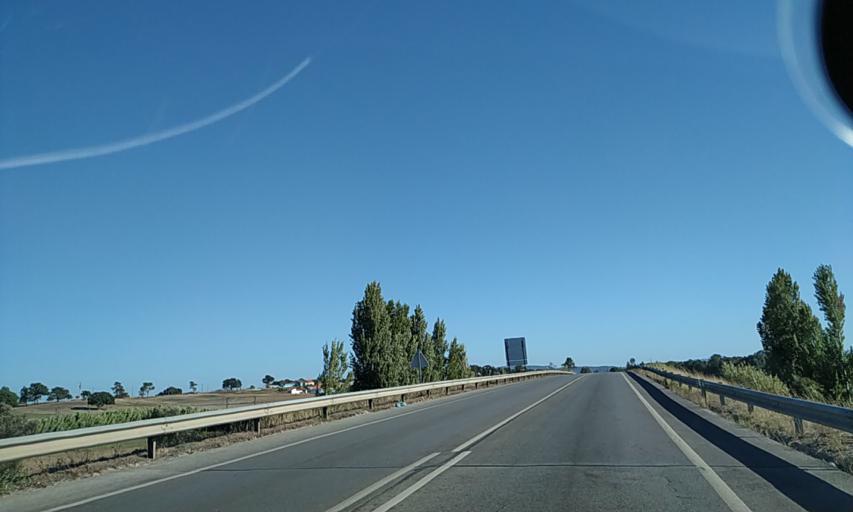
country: PT
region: Setubal
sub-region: Moita
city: Moita
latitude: 38.6416
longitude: -8.9718
